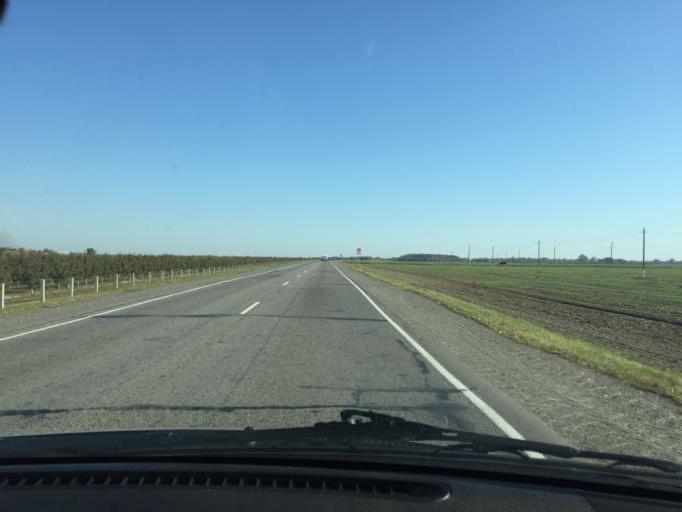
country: BY
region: Gomel
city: Turaw
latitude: 52.0601
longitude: 27.8016
